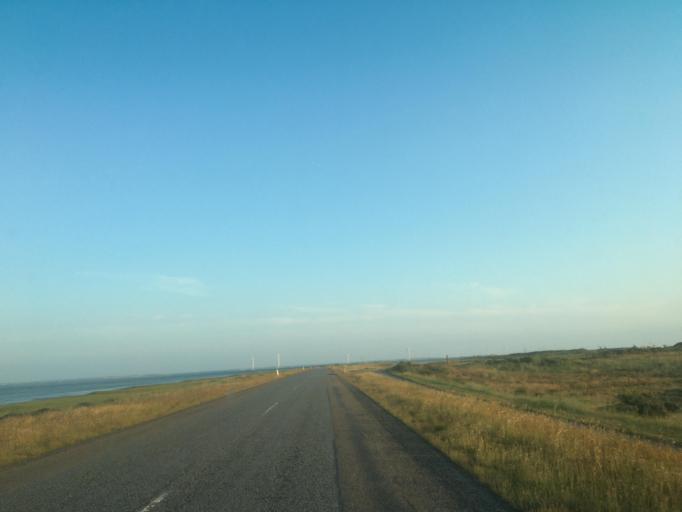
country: DK
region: Central Jutland
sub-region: Lemvig Kommune
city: Thyboron
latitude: 56.7164
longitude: 8.2488
